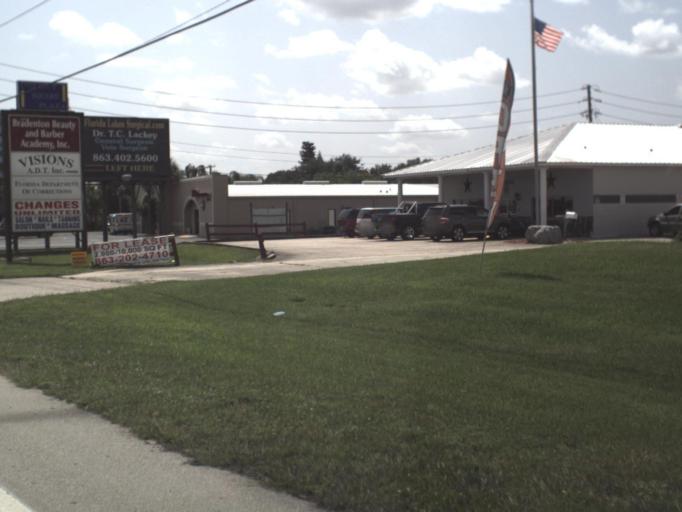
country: US
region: Florida
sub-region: Highlands County
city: Sebring
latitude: 27.4839
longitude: -81.4796
